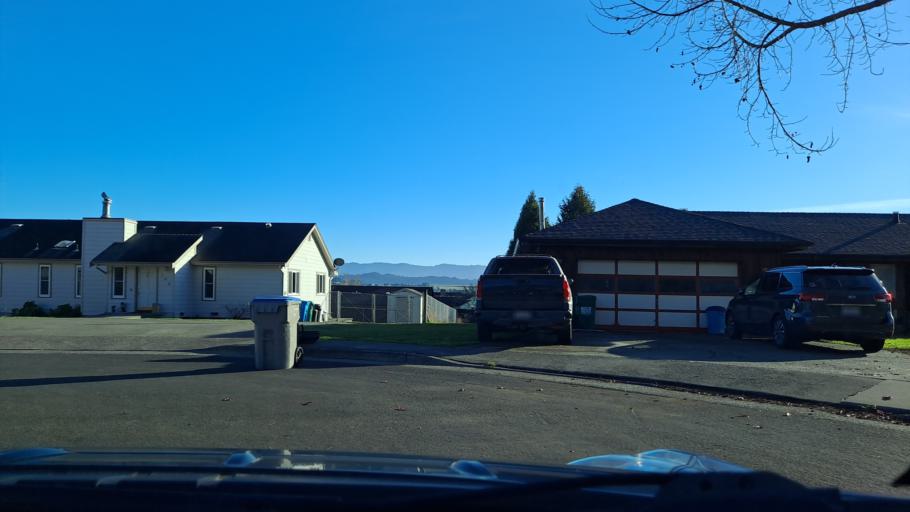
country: US
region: California
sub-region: Humboldt County
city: Fortuna
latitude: 40.5966
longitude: -124.1400
